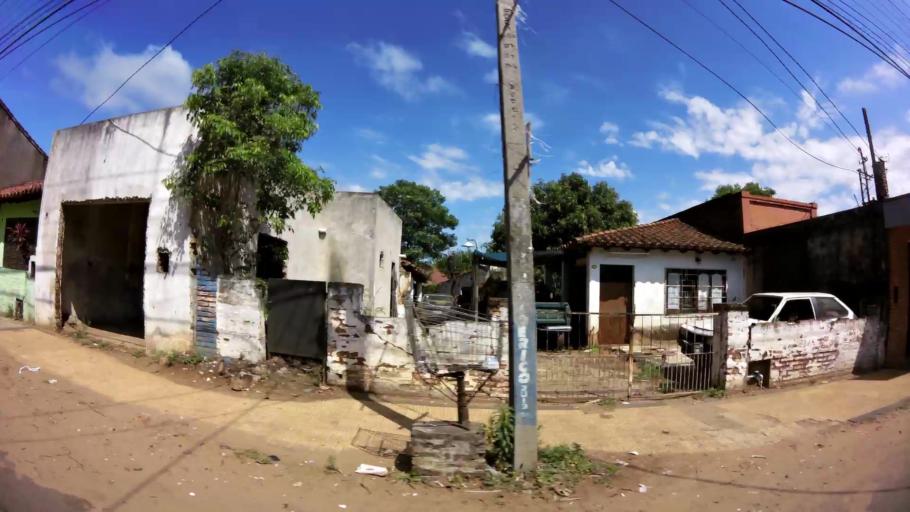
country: PY
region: Central
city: San Lorenzo
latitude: -25.2604
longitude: -57.4905
